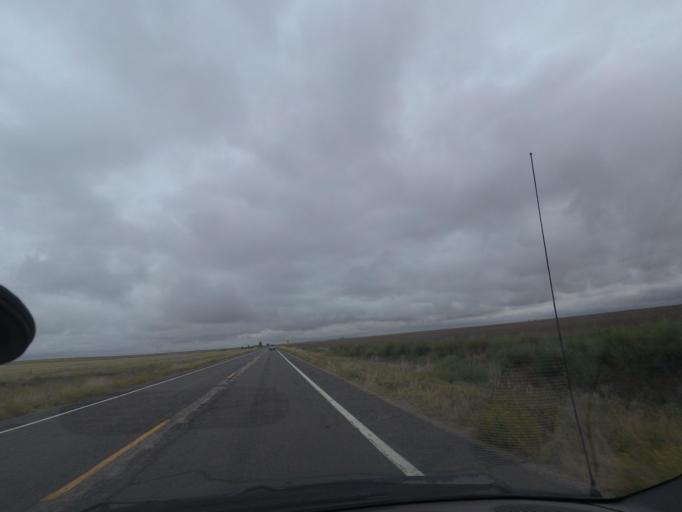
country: US
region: Colorado
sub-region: Washington County
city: Akron
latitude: 39.7027
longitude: -103.0717
